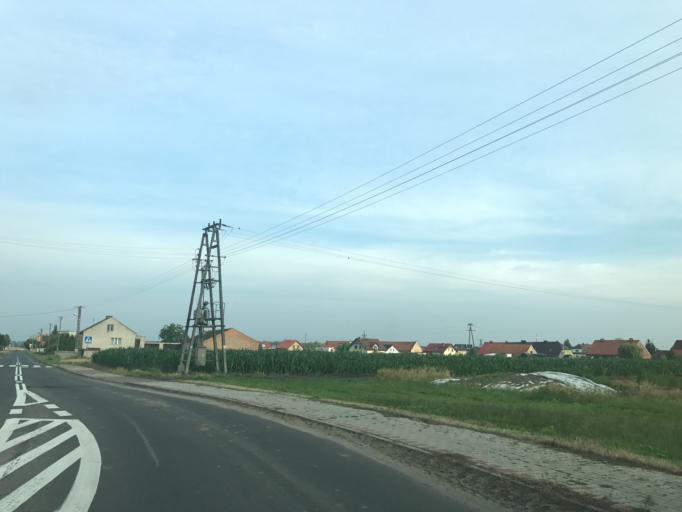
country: PL
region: Greater Poland Voivodeship
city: Miejska Gorka
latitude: 51.6326
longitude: 16.9652
